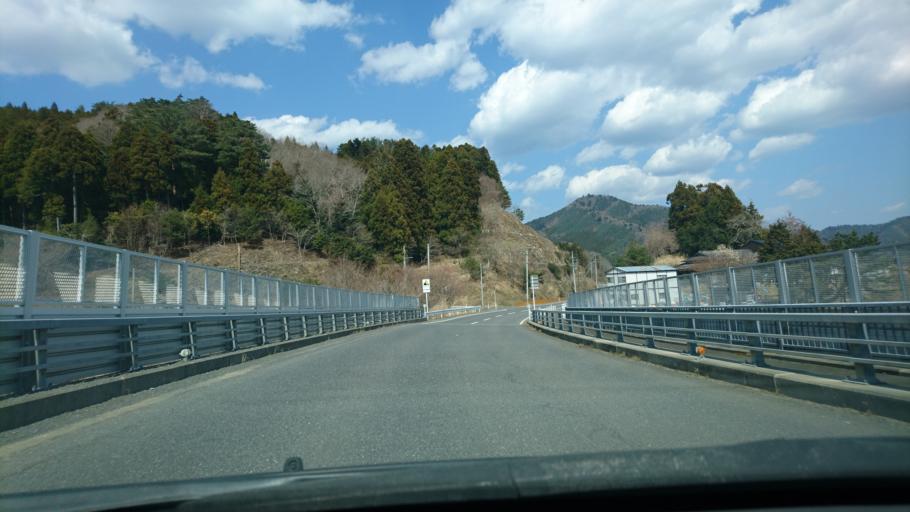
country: JP
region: Miyagi
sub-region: Oshika Gun
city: Onagawa Cho
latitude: 38.5036
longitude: 141.4848
